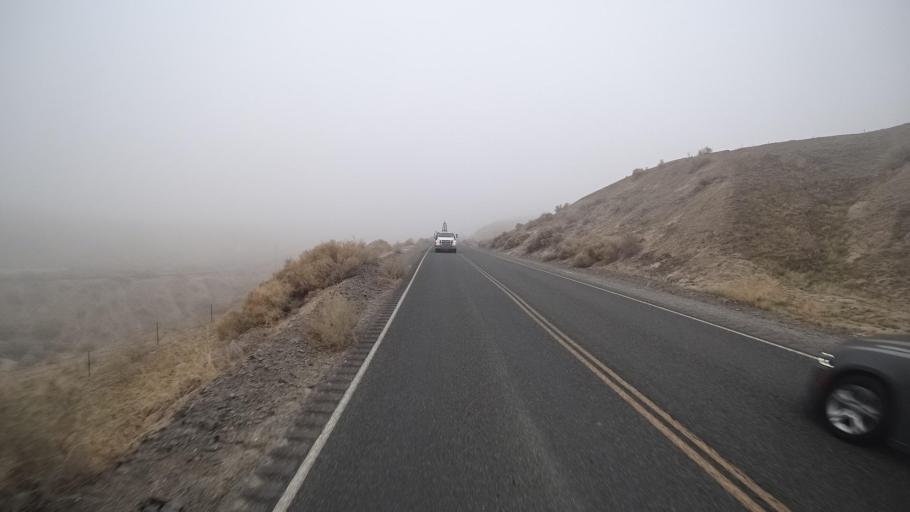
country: US
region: California
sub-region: Kern County
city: Buttonwillow
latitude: 35.2882
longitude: -119.4652
